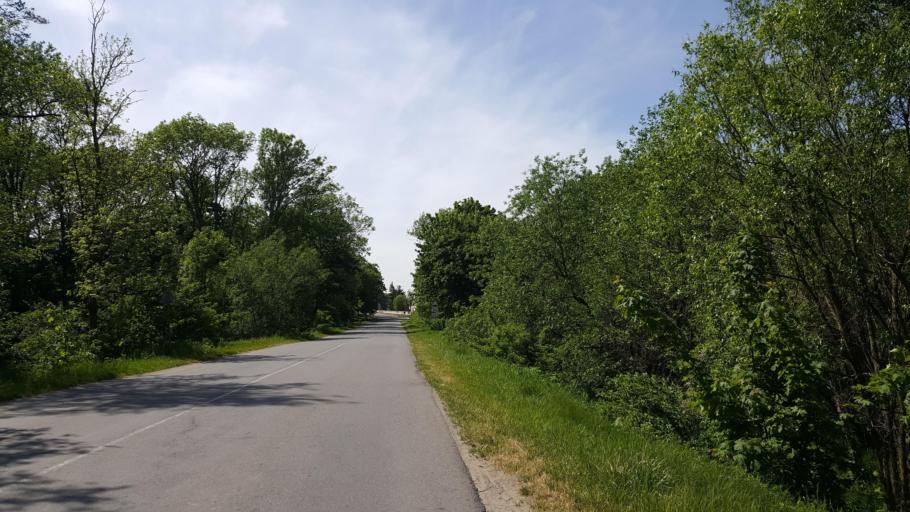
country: BY
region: Brest
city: Charnawchytsy
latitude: 52.2034
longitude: 23.6924
